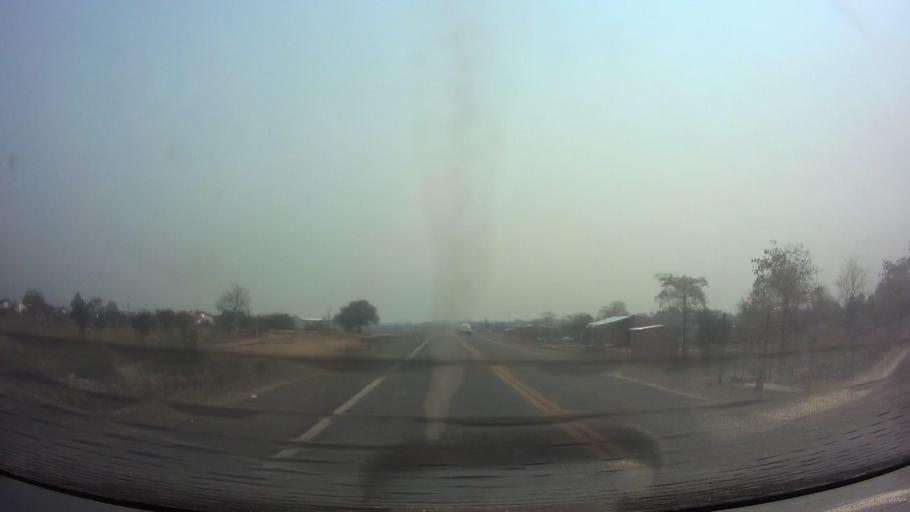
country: PY
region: Central
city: Limpio
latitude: -25.1528
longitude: -57.4813
